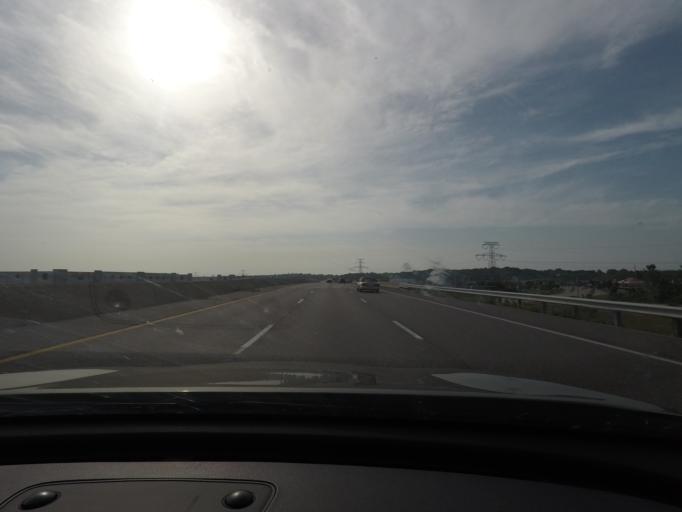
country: US
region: Missouri
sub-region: Saint Charles County
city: Saint Charles
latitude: 38.8244
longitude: -90.5192
